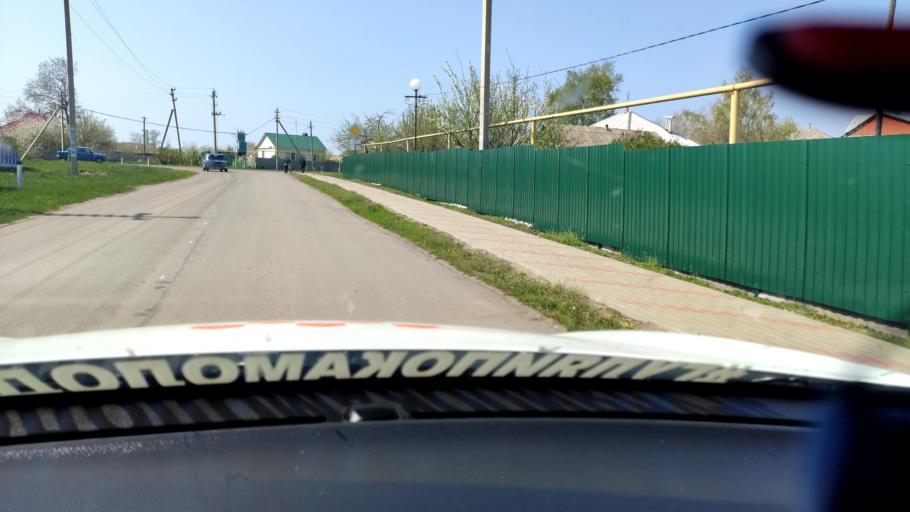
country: RU
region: Voronezj
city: Uryv-Pokrovka
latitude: 51.0764
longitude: 39.1175
